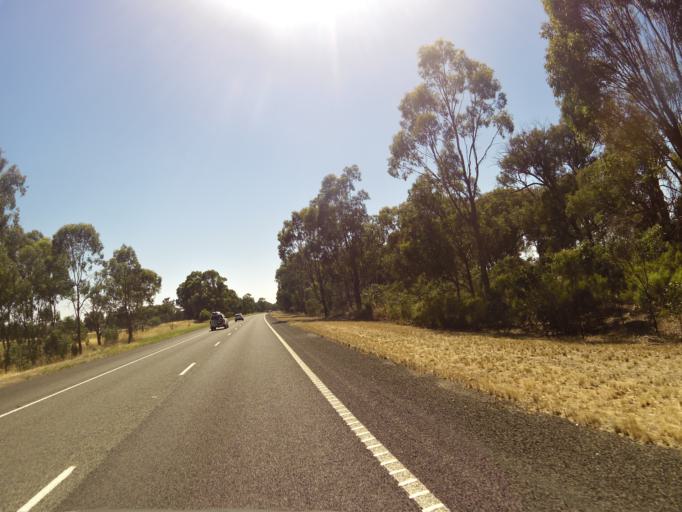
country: AU
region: Victoria
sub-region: Greater Shepparton
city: Shepparton
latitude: -36.8639
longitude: 145.3001
